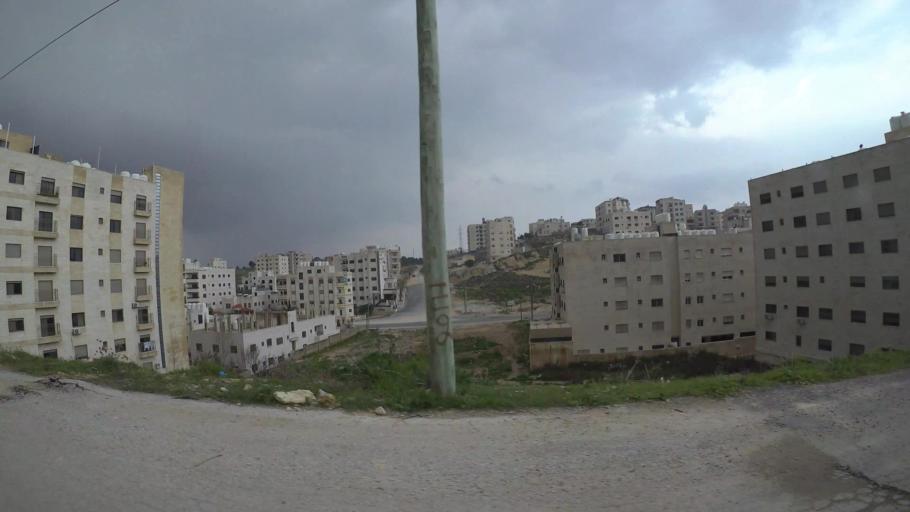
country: JO
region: Amman
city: Umm as Summaq
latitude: 31.8819
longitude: 35.8547
